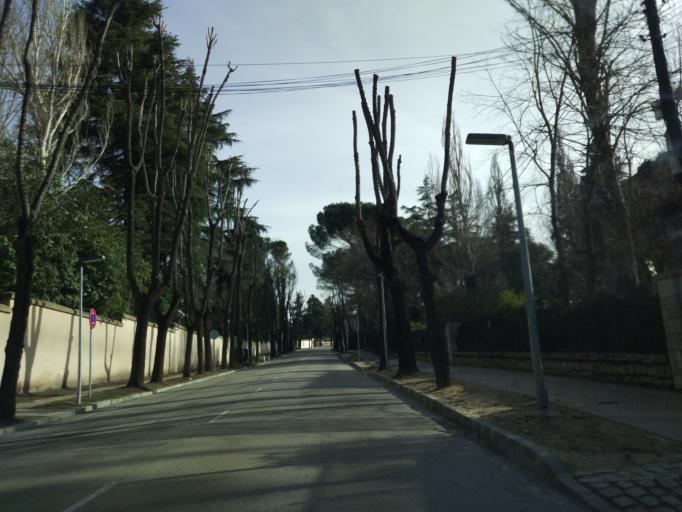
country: ES
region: Madrid
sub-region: Provincia de Madrid
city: Tetuan de las Victorias
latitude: 40.4698
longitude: -3.7316
